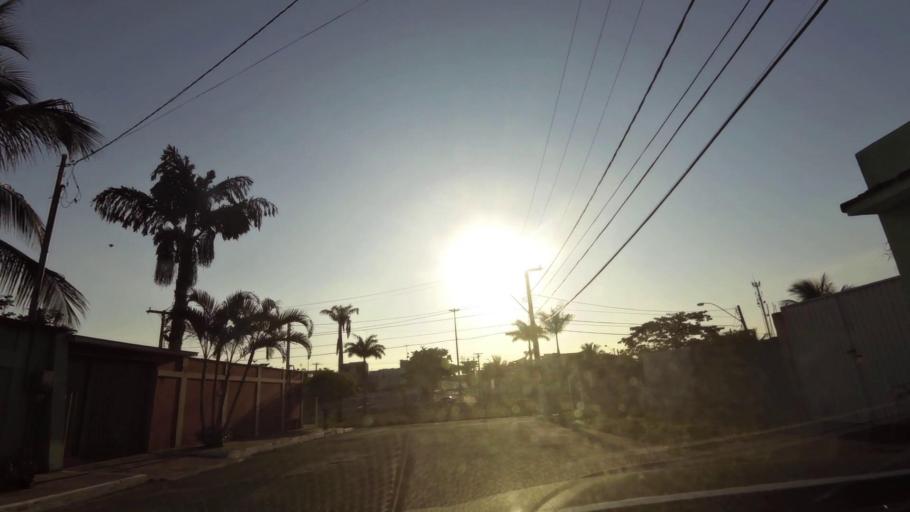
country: BR
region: Espirito Santo
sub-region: Vila Velha
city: Vila Velha
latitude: -20.4846
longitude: -40.3504
